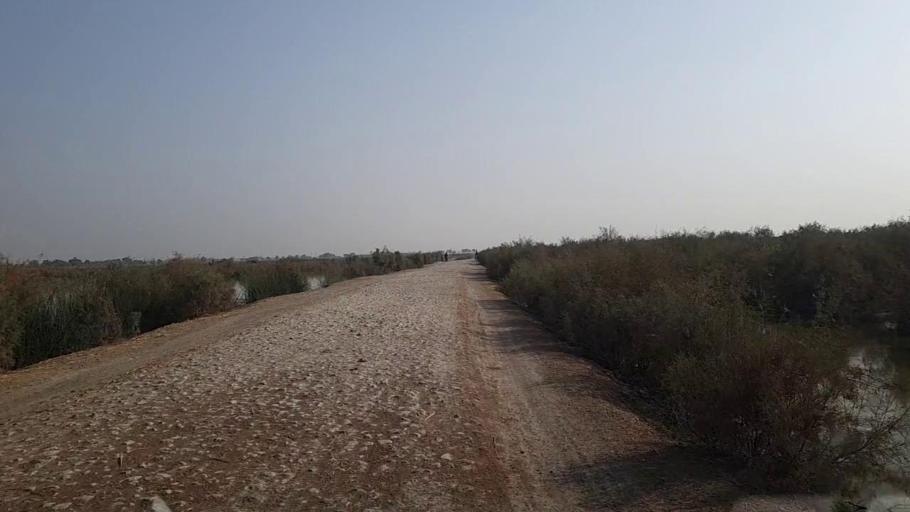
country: PK
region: Sindh
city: Kandhkot
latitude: 28.2941
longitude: 69.2530
